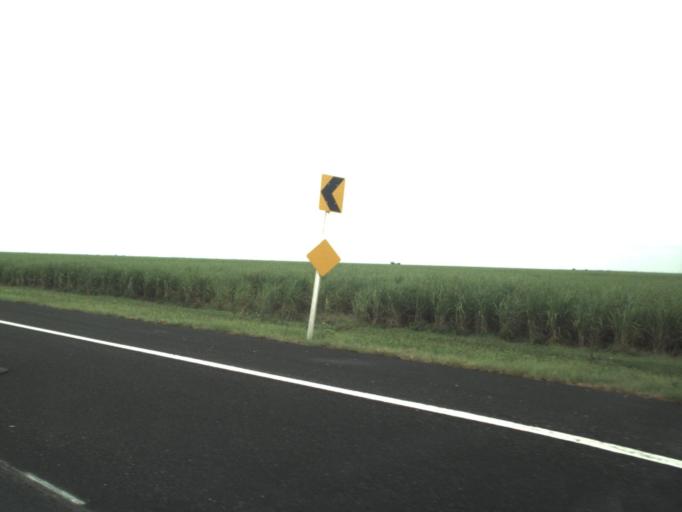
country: US
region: Florida
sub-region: Palm Beach County
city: Loxahatchee Groves
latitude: 26.7238
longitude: -80.4378
